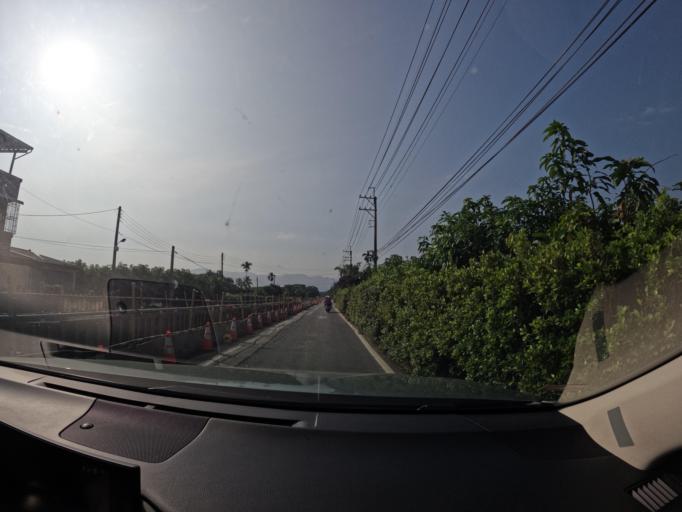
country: TW
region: Taiwan
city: Yujing
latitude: 23.1015
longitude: 120.4811
